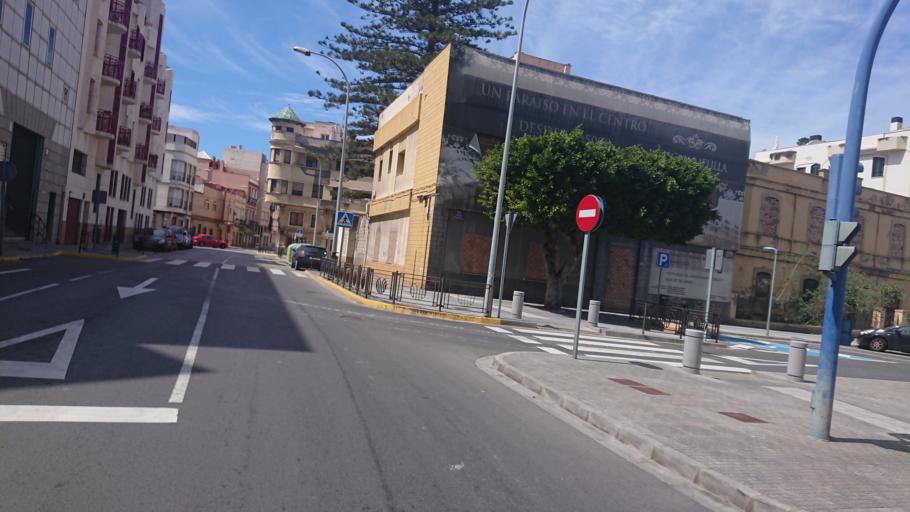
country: ES
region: Melilla
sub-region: Melilla
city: Melilla
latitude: 35.2898
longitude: -2.9398
